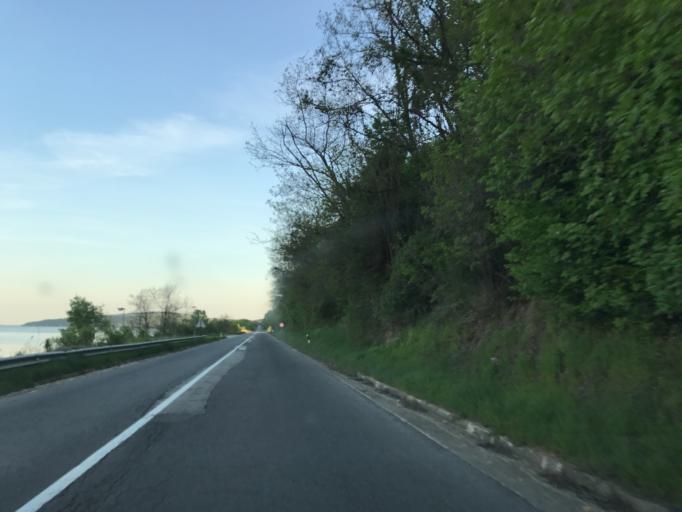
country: RO
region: Mehedinti
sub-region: Comuna Gogosu
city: Ostrovu Mare
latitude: 44.4649
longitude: 22.4505
